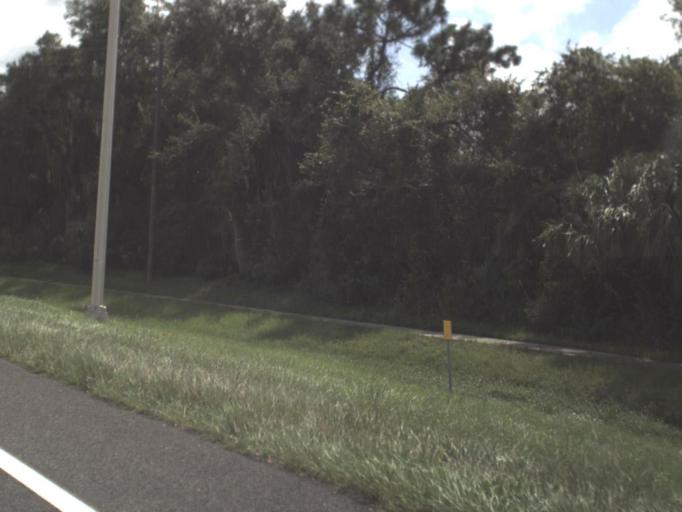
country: US
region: Florida
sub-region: Sarasota County
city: The Meadows
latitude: 27.4769
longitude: -82.4018
